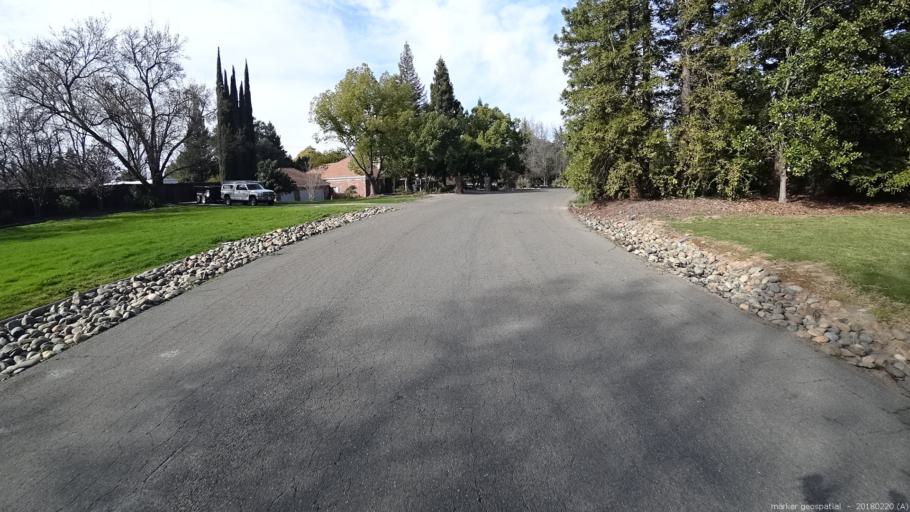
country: US
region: California
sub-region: Sacramento County
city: Orangevale
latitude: 38.7099
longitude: -121.2414
